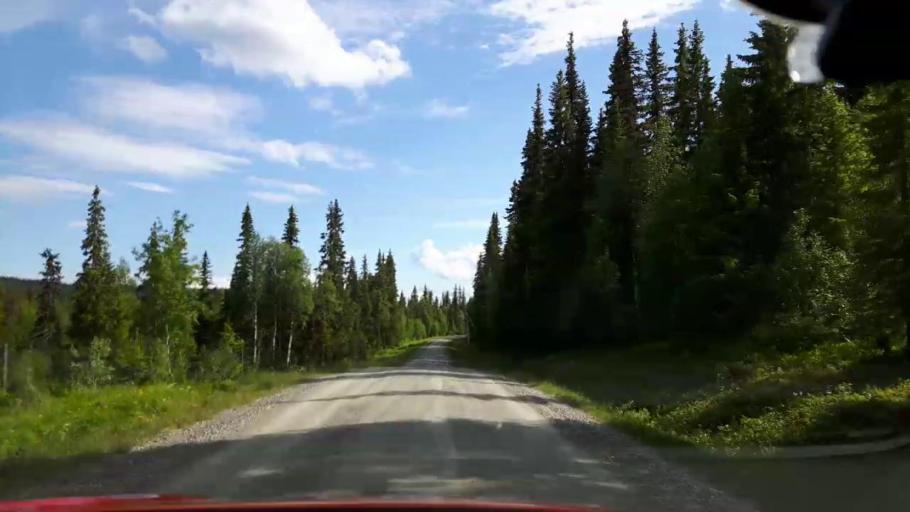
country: SE
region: Jaemtland
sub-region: Krokoms Kommun
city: Valla
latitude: 63.8091
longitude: 14.0497
